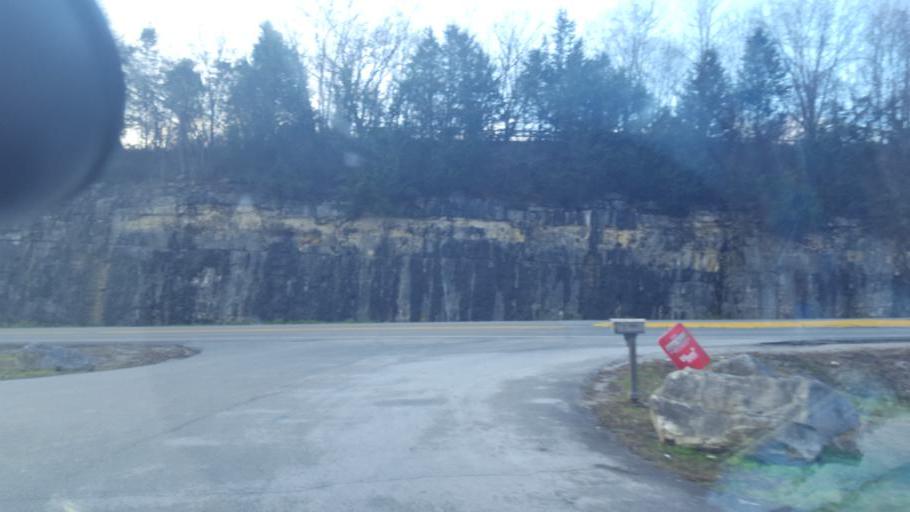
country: US
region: Kentucky
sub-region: Rockcastle County
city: Mount Vernon
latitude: 37.3415
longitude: -84.3054
